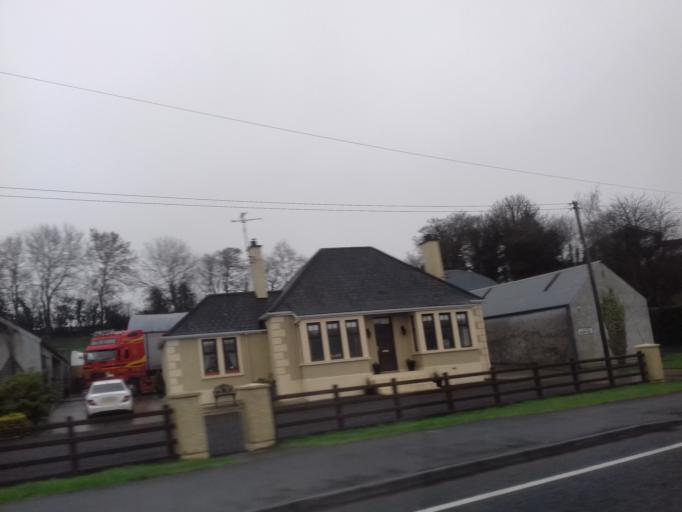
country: GB
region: Northern Ireland
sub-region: Strabane District
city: Sion Mills
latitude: 54.7637
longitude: -7.4636
